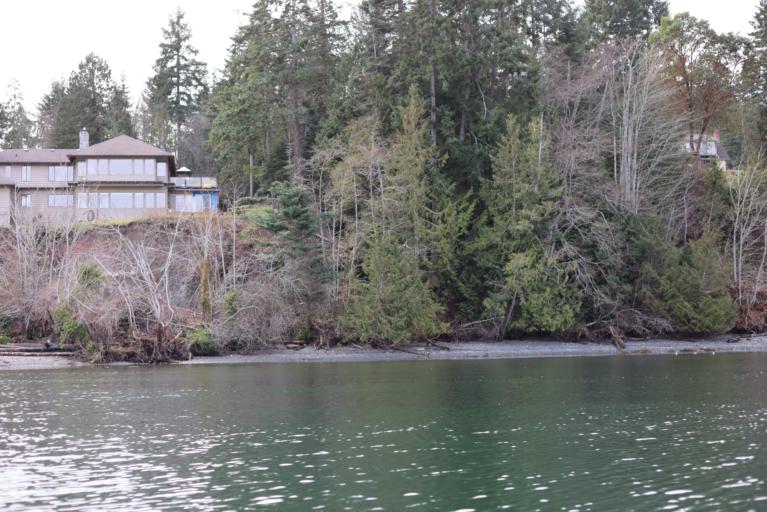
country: CA
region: British Columbia
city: Duncan
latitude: 48.7364
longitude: -123.5942
